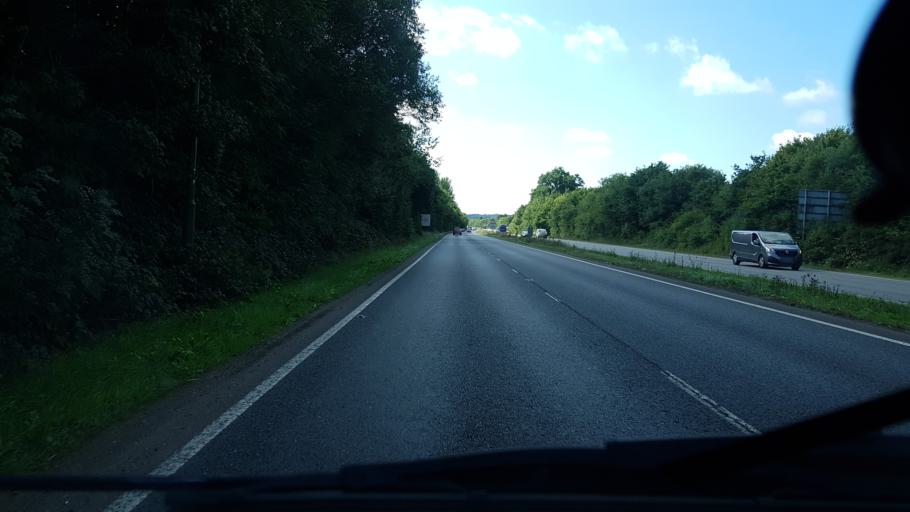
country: GB
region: England
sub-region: West Sussex
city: Horsham
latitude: 51.0878
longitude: -0.3058
